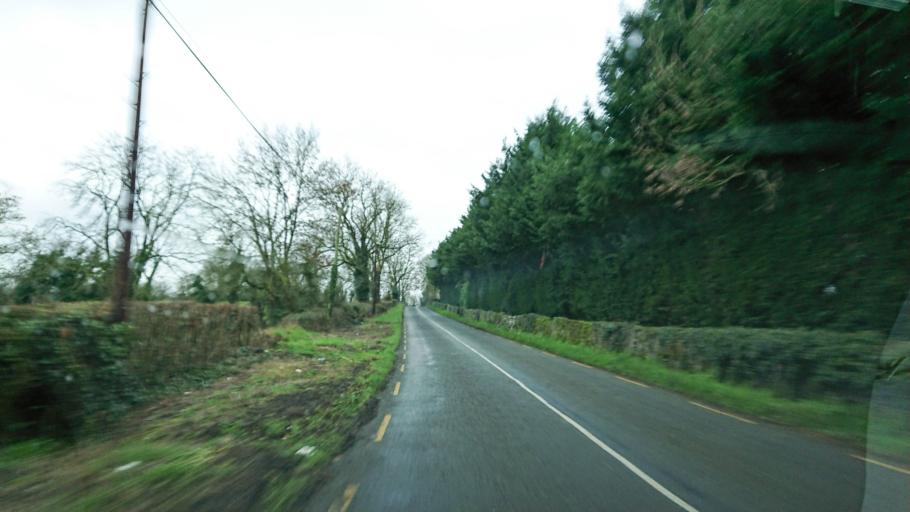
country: IE
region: Leinster
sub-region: Kilkenny
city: Callan
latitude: 52.5357
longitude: -7.2926
